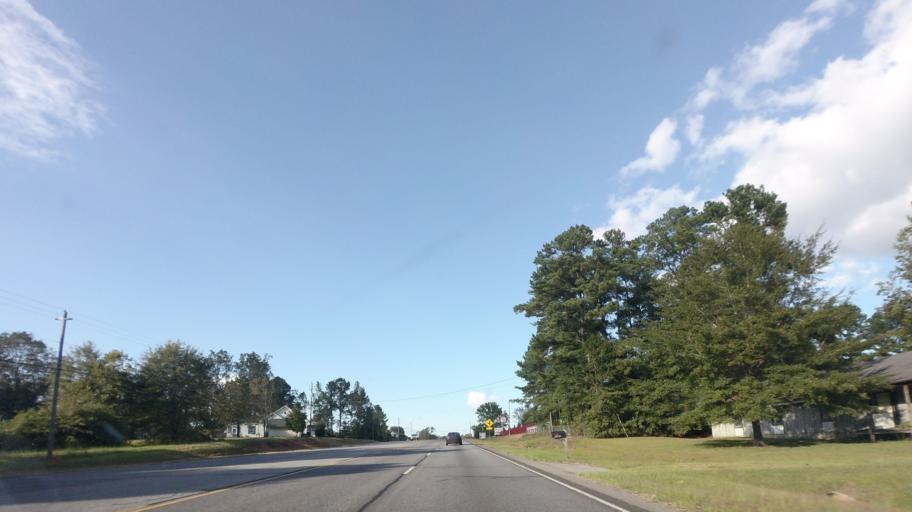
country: US
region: Georgia
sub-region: Upson County
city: Hannahs Mill
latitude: 32.9608
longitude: -84.3325
